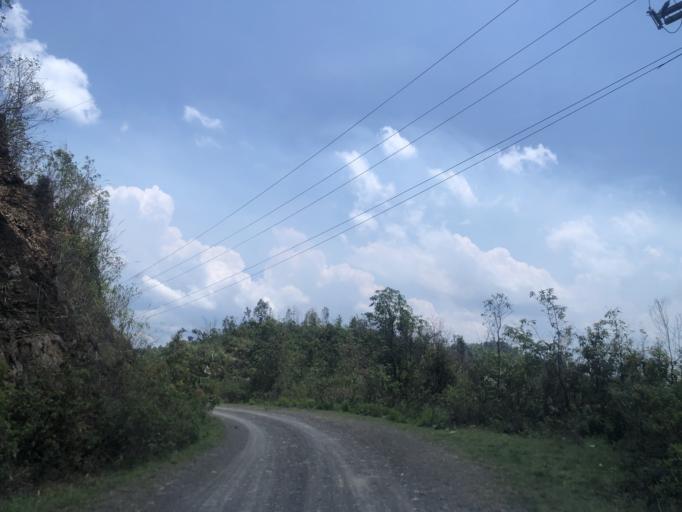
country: LA
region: Phongsali
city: Phongsali
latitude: 21.4342
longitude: 102.1622
